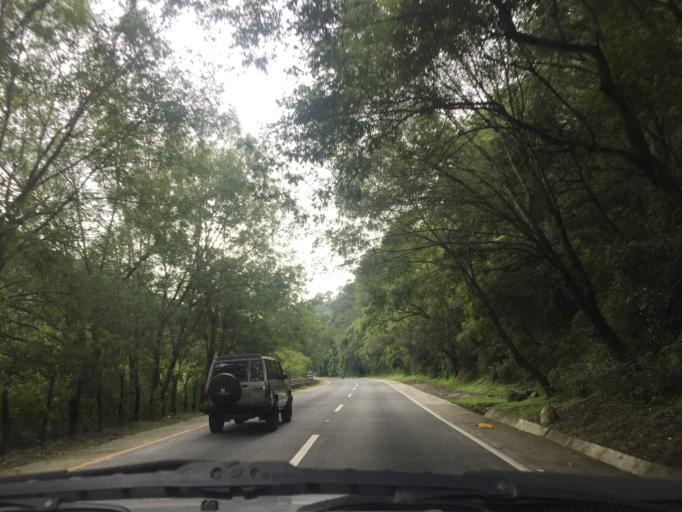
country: GT
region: Sacatepequez
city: Santa Lucia Milpas Altas
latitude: 14.5627
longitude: -90.6941
